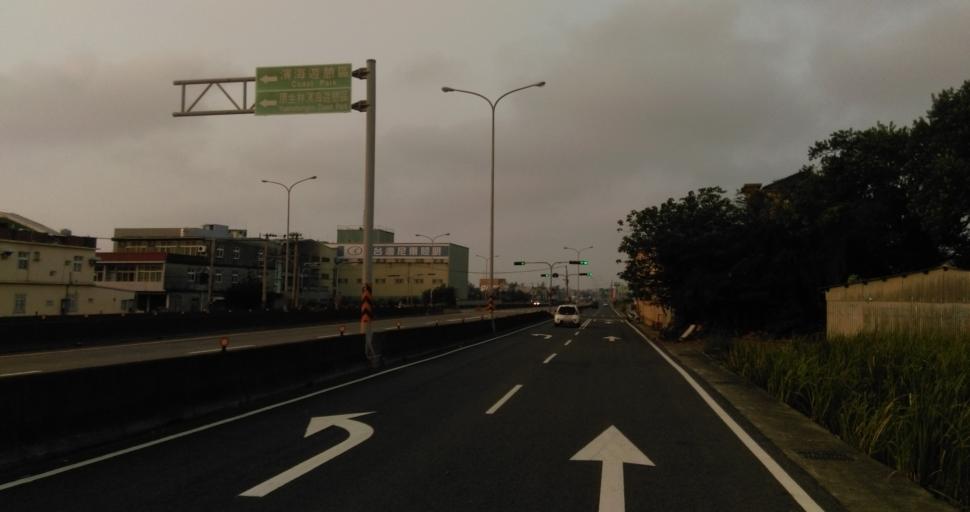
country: TW
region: Taiwan
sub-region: Hsinchu
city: Zhubei
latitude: 24.8674
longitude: 120.9534
